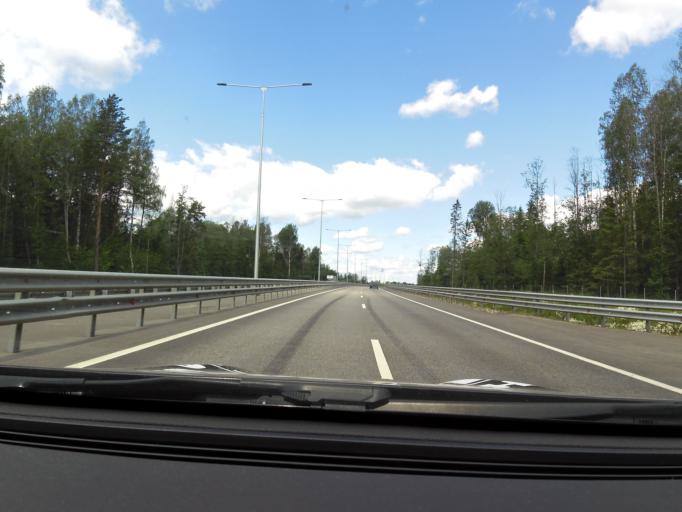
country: RU
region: Tverskaya
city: Vydropuzhsk
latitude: 57.2880
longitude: 34.7871
